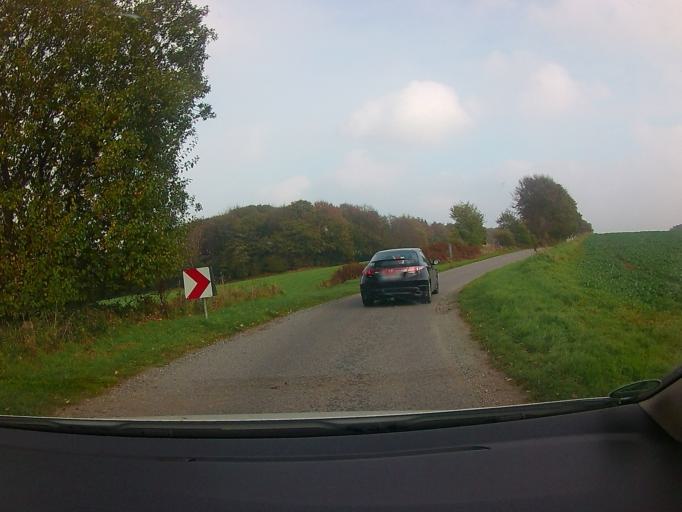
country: DE
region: Schleswig-Holstein
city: Wees
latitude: 54.8622
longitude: 9.4844
